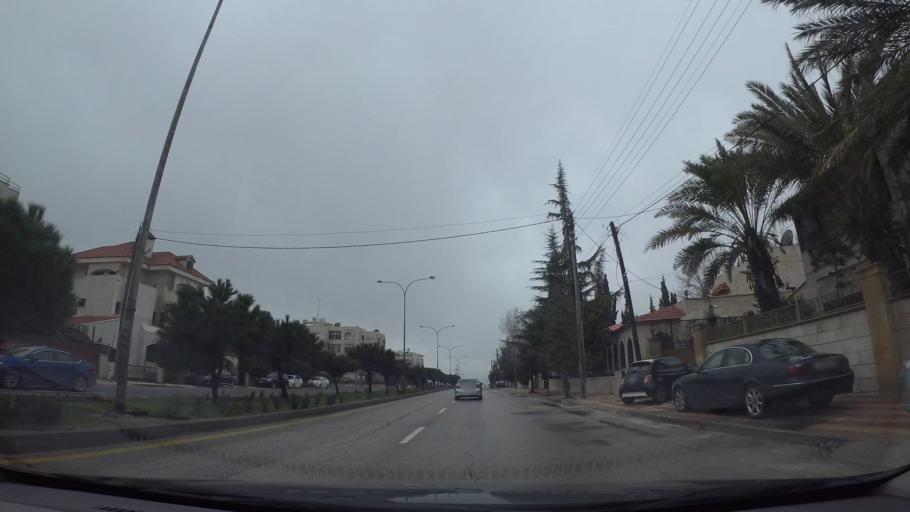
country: JO
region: Amman
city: Wadi as Sir
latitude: 31.9459
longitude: 35.8633
